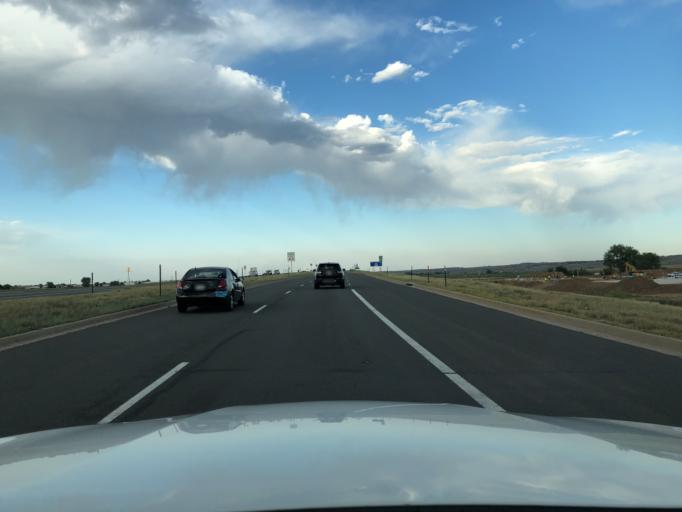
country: US
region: Colorado
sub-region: Boulder County
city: Louisville
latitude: 39.9494
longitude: -105.1246
